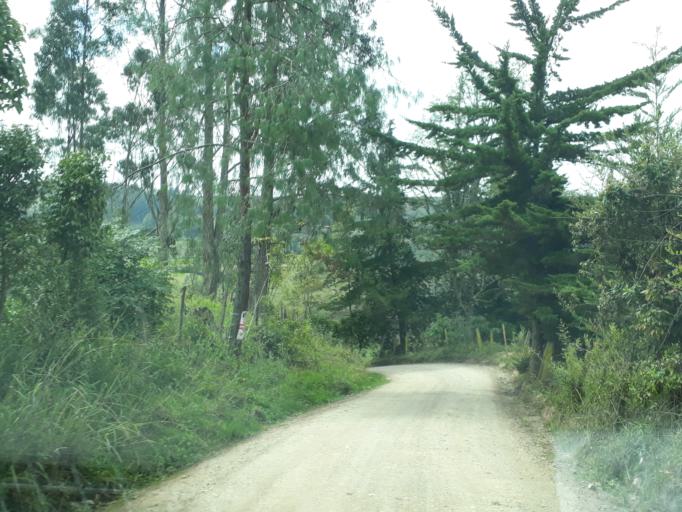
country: CO
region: Cundinamarca
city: Macheta
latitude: 5.0921
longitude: -73.5686
